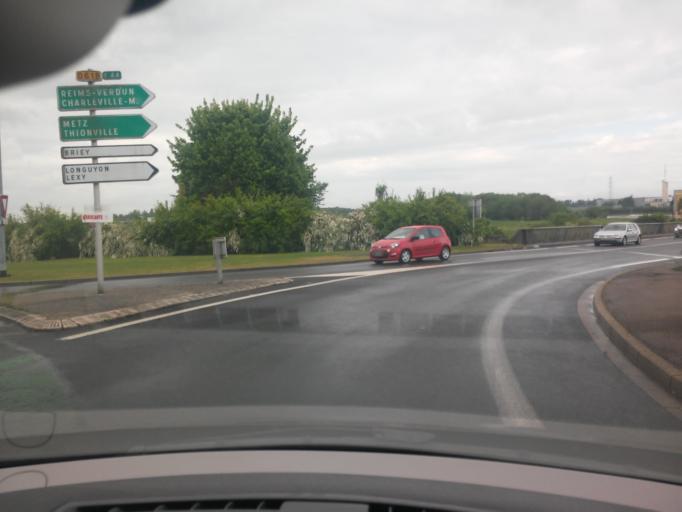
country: FR
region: Lorraine
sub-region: Departement de Meurthe-et-Moselle
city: Rehon
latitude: 49.5182
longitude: 5.7514
